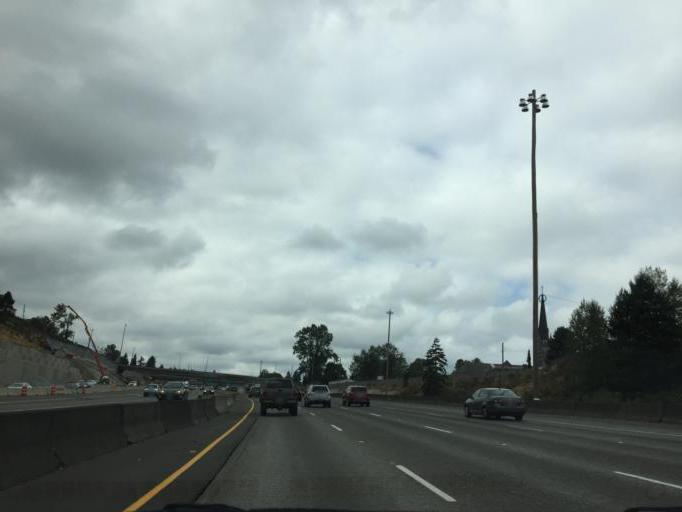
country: US
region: Washington
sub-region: Pierce County
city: Tacoma
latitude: 47.2330
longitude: -122.4360
